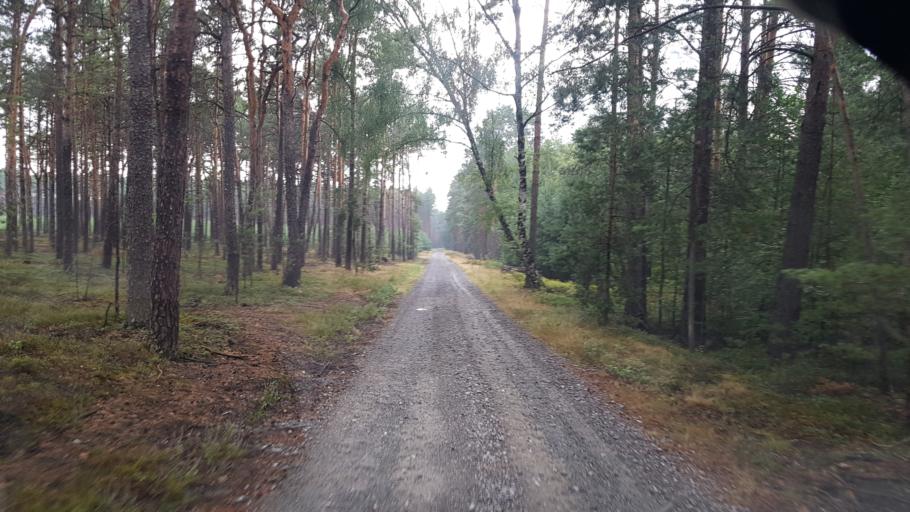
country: DE
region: Brandenburg
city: Sallgast
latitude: 51.6295
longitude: 13.7988
